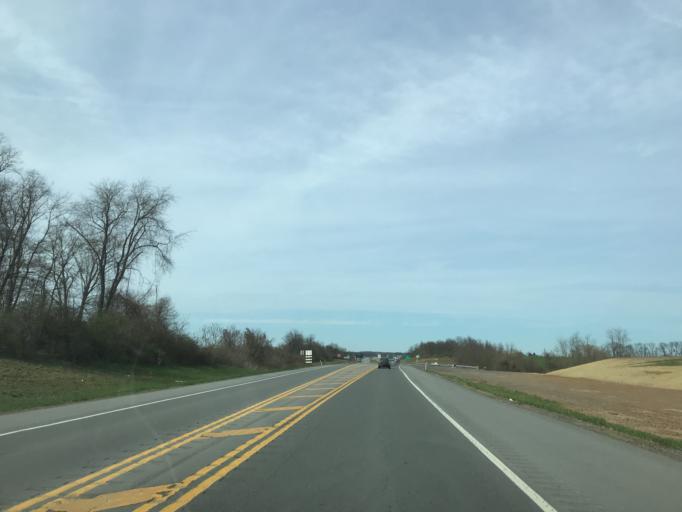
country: US
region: Pennsylvania
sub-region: Union County
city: Lewisburg
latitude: 40.9509
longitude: -76.8522
